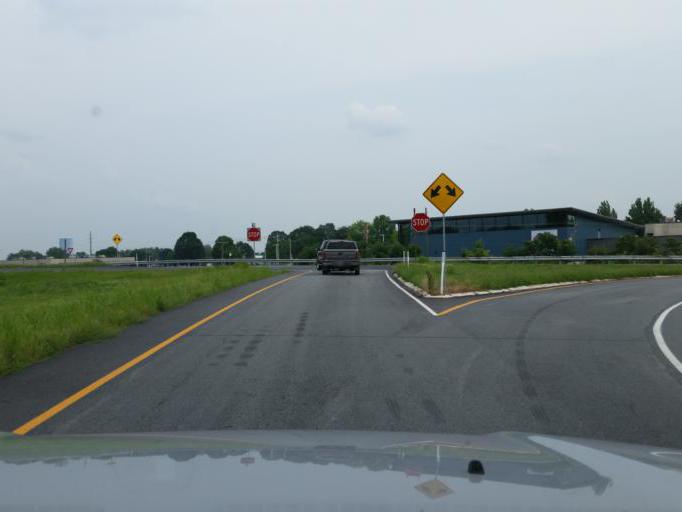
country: US
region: Pennsylvania
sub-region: Lancaster County
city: Mount Joy
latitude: 40.1247
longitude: -76.4709
